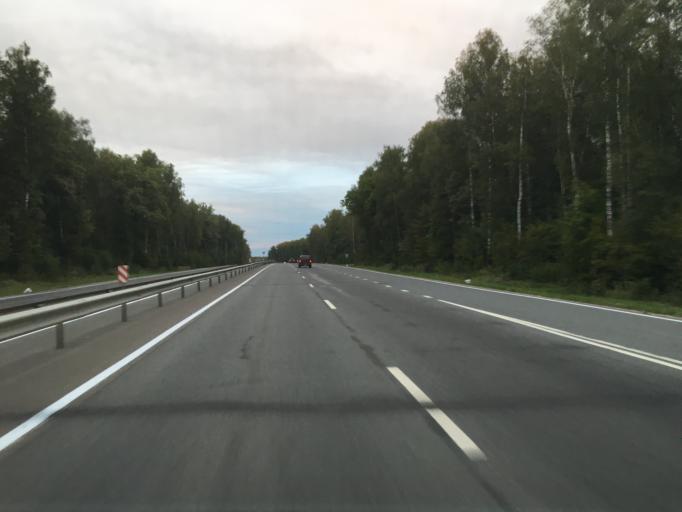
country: RU
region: Kaluga
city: Kaluga
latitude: 54.5763
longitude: 36.3353
